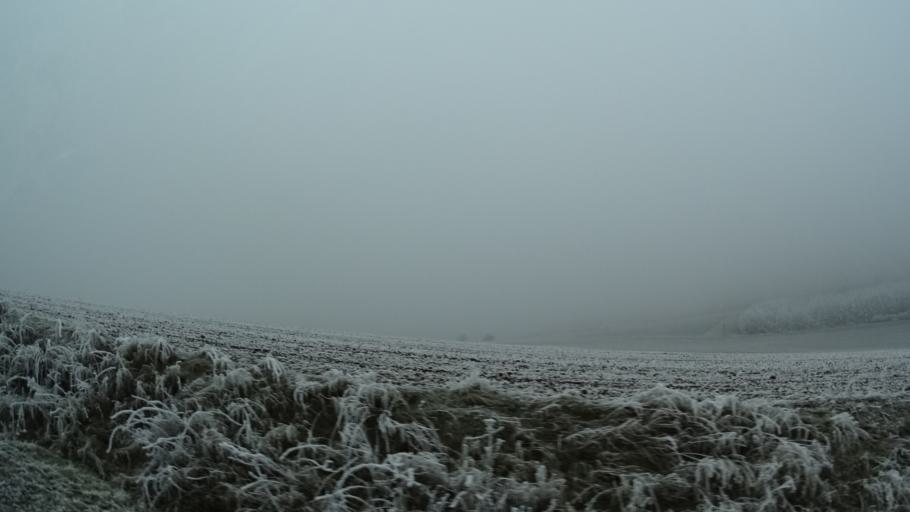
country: DE
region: Thuringia
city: Henneberg
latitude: 50.5195
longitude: 10.3286
